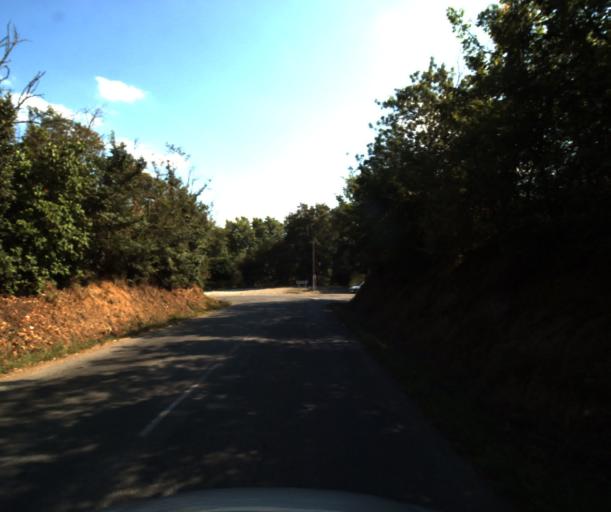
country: FR
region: Midi-Pyrenees
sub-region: Departement de la Haute-Garonne
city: Saint-Lys
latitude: 43.5177
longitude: 1.1796
